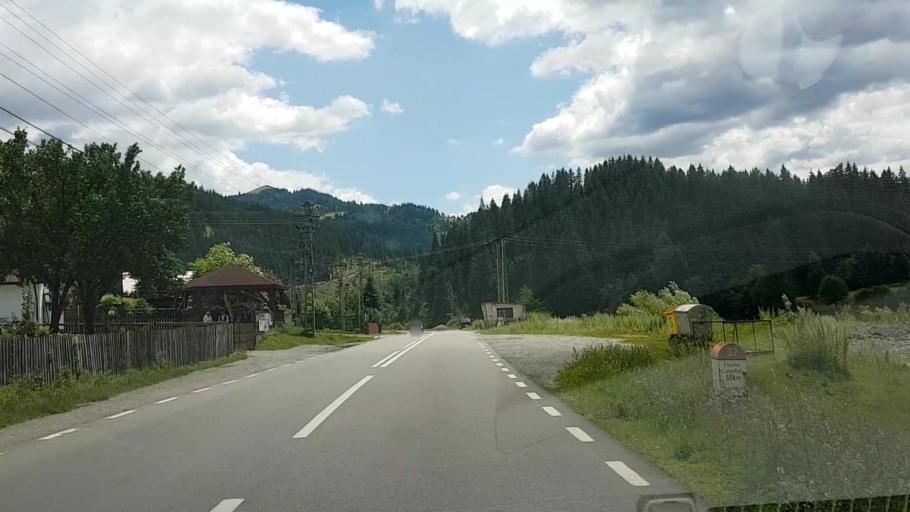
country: RO
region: Suceava
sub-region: Comuna Crucea
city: Crucea
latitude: 47.3593
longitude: 25.6088
